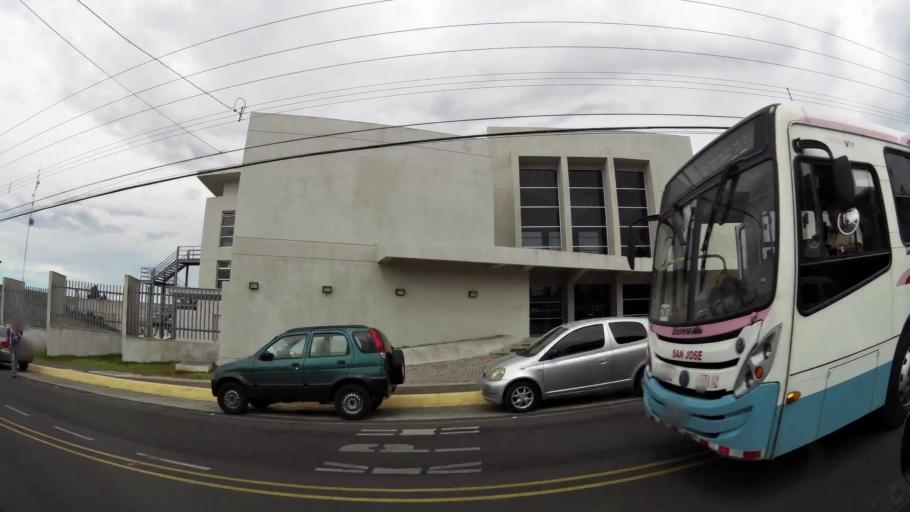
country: CR
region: San Jose
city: Ipis
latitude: 9.9703
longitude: -84.0153
